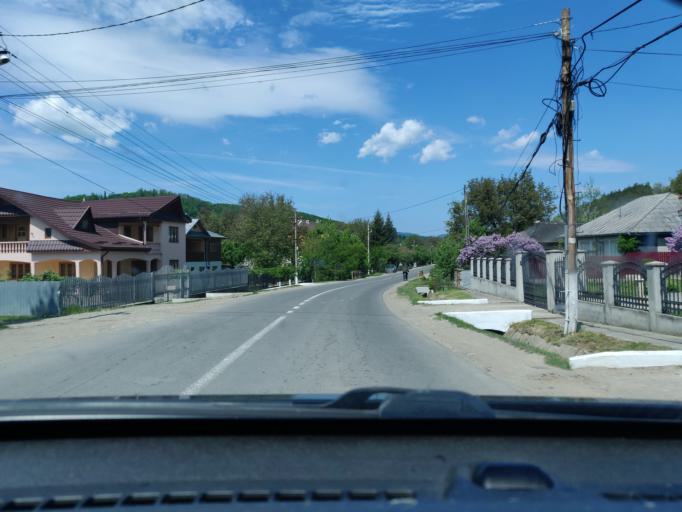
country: RO
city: Campurile de Jos
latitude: 46.0248
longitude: 26.7675
